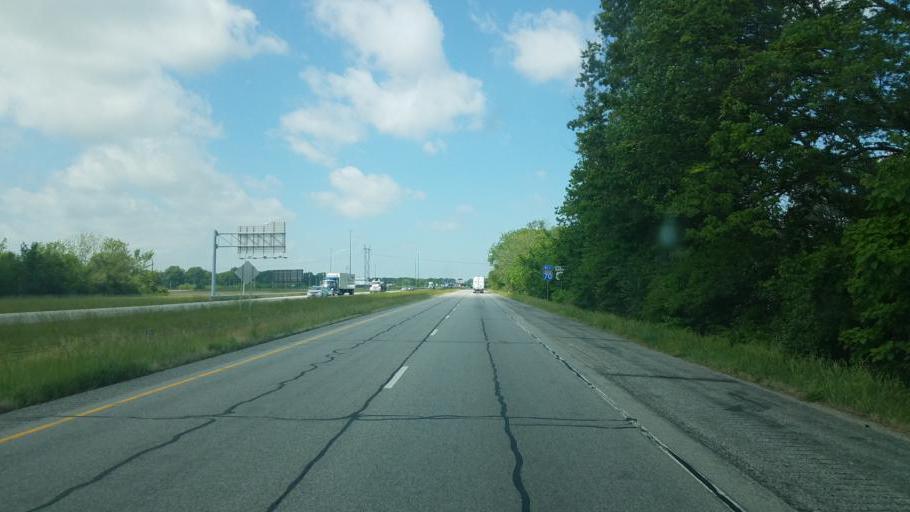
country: US
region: Indiana
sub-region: Vigo County
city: West Terre Haute
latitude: 39.4391
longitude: -87.5204
